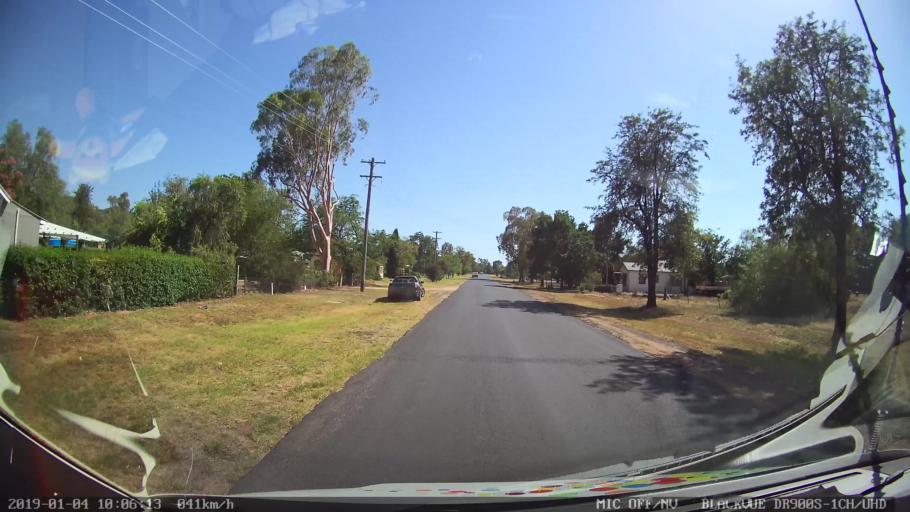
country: AU
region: New South Wales
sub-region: Cabonne
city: Canowindra
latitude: -33.4350
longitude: 148.3677
